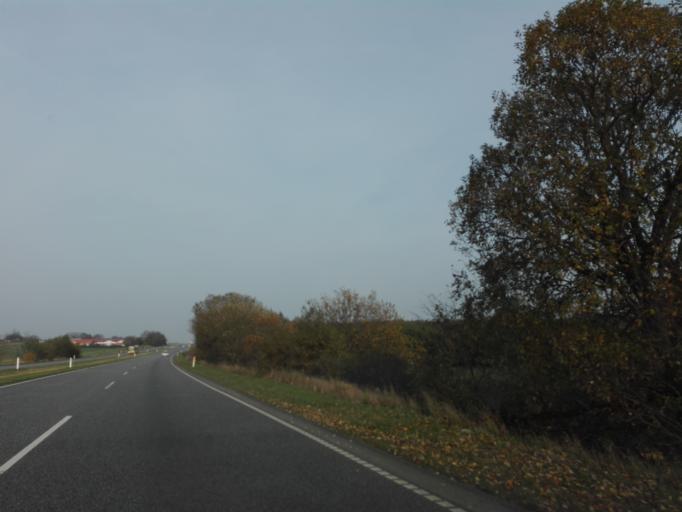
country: DK
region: Central Jutland
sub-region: Arhus Kommune
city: Solbjerg
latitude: 56.0476
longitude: 10.0821
